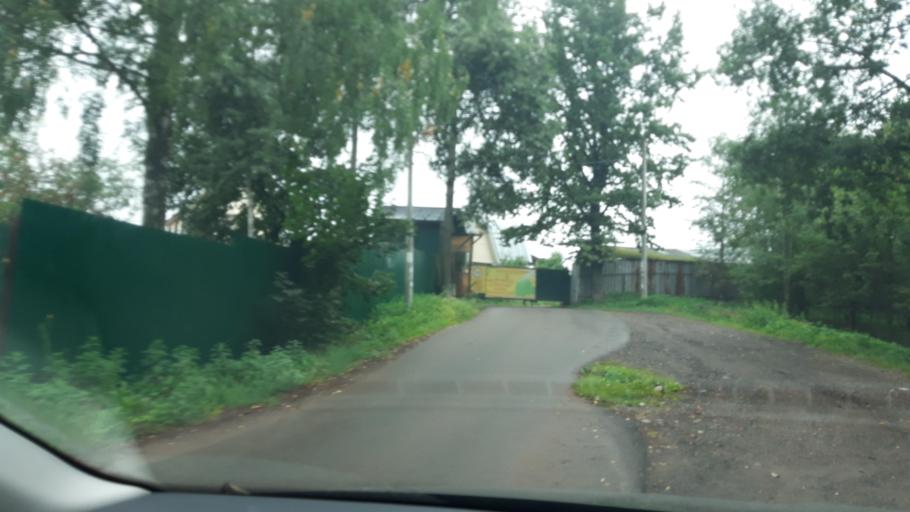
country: RU
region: Moskovskaya
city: Novopodrezkovo
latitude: 55.9251
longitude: 37.3398
